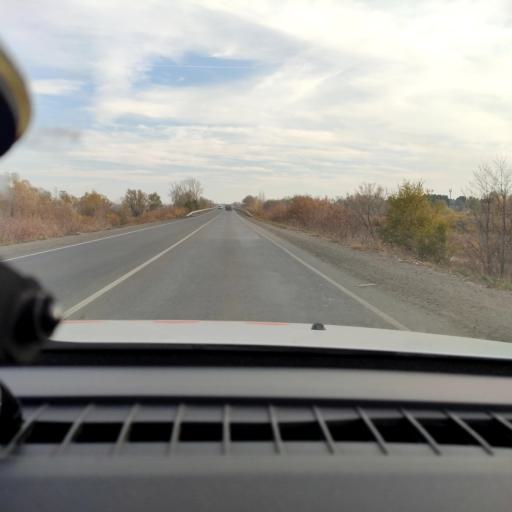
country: RU
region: Samara
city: Samara
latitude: 53.1039
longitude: 50.1378
